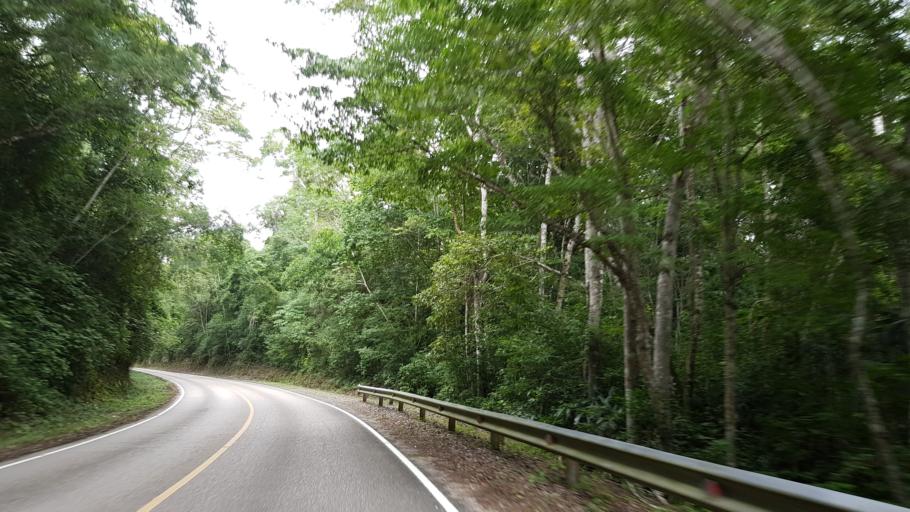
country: GT
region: Peten
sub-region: Municipio de San Jose
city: San Jose
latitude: 17.2145
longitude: -89.6122
